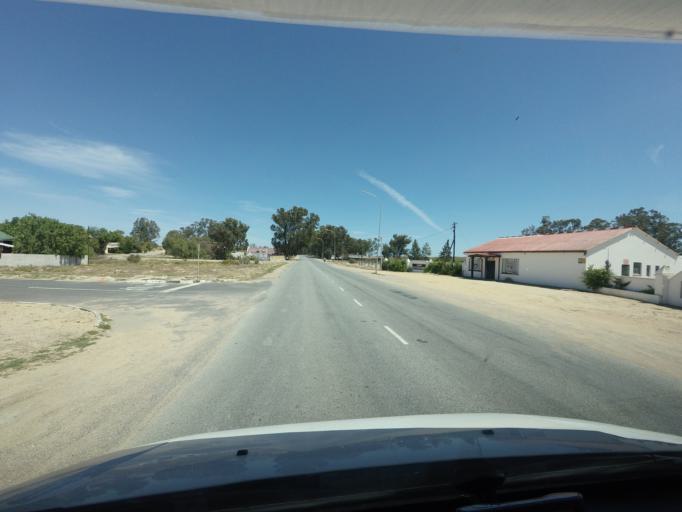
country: ZA
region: Western Cape
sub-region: West Coast District Municipality
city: Vredenburg
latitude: -32.7895
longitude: 18.2042
